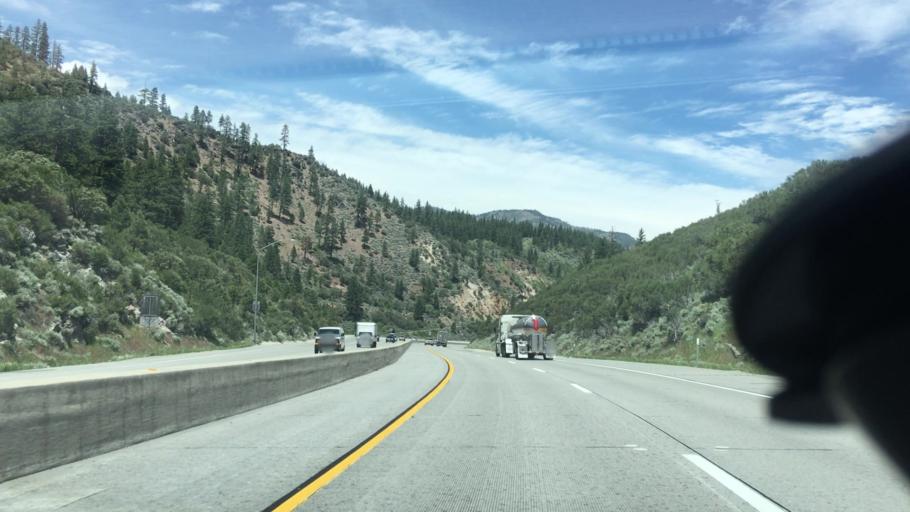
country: US
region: Nevada
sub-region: Washoe County
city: Verdi
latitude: 39.3896
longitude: -120.0247
